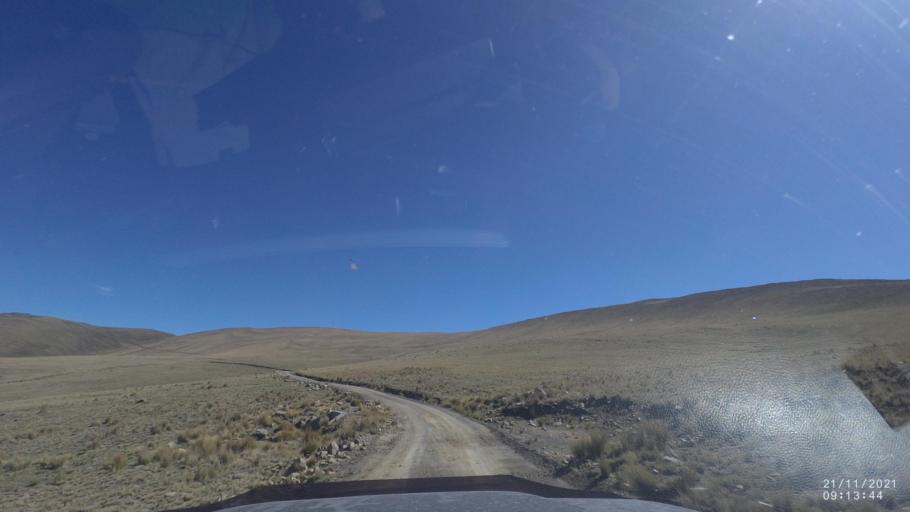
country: BO
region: Cochabamba
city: Cochabamba
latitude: -17.1389
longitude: -66.2578
